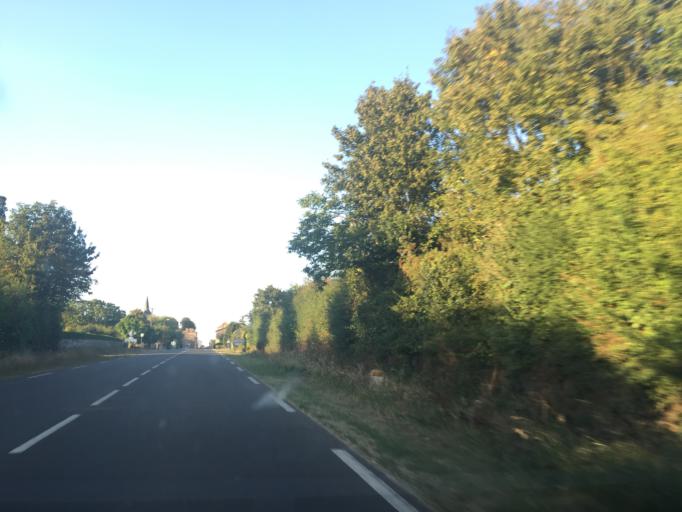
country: FR
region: Poitou-Charentes
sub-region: Departement des Deux-Sevres
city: Lezay
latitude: 46.3222
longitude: -0.0365
